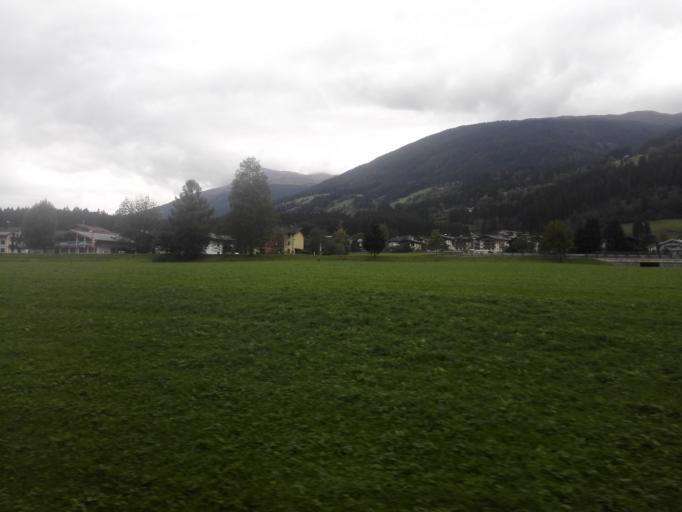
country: AT
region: Salzburg
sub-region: Politischer Bezirk Zell am See
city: Neukirchen am Grossvenediger
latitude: 47.2499
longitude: 12.2791
